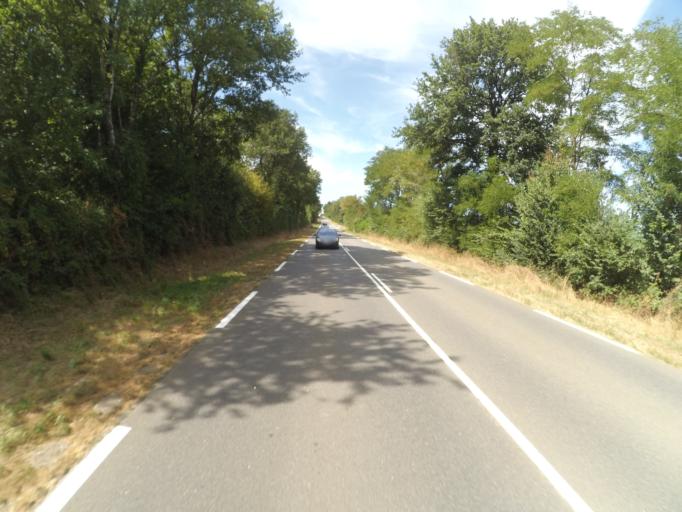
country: FR
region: Poitou-Charentes
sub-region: Departement de la Charente
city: Confolens
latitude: 45.9791
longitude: 0.6838
